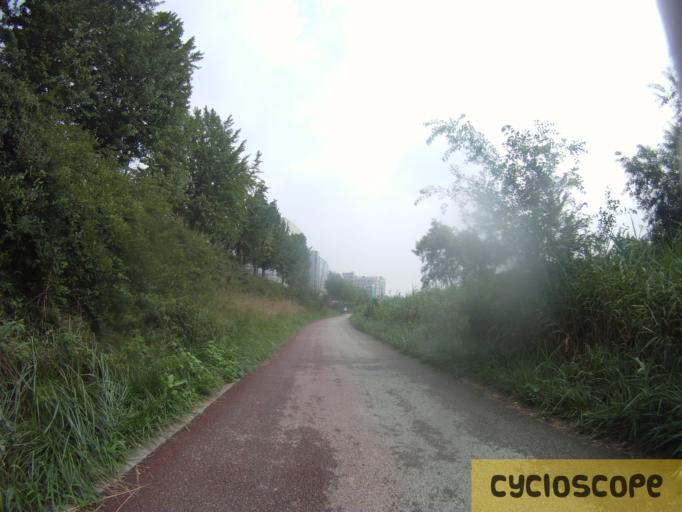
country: KR
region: Gyeonggi-do
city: Anyang-si
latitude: 37.3914
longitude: 126.9415
